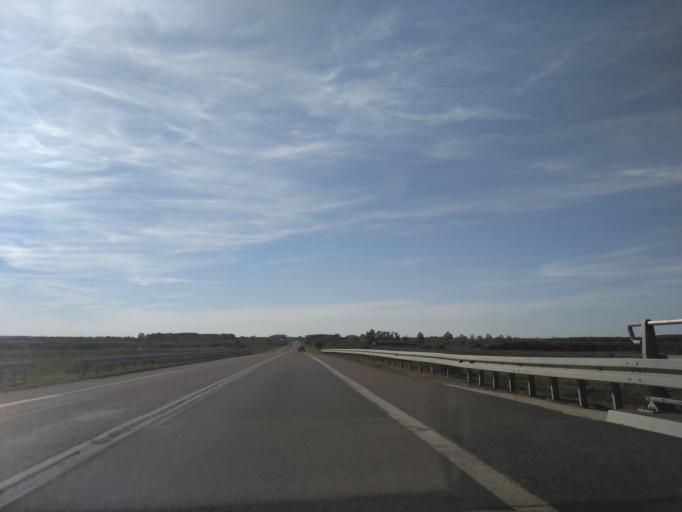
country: PL
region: Lublin Voivodeship
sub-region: Powiat swidnicki
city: Trawniki
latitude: 51.1649
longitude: 23.0515
